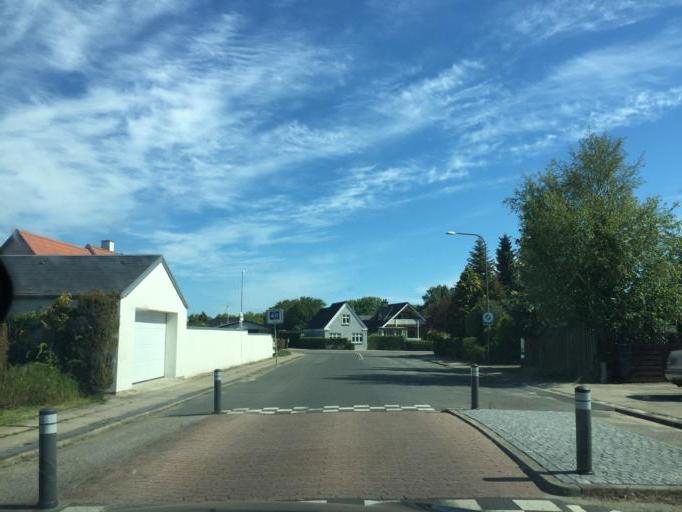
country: DK
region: South Denmark
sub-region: Kerteminde Kommune
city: Langeskov
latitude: 55.3564
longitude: 10.5951
